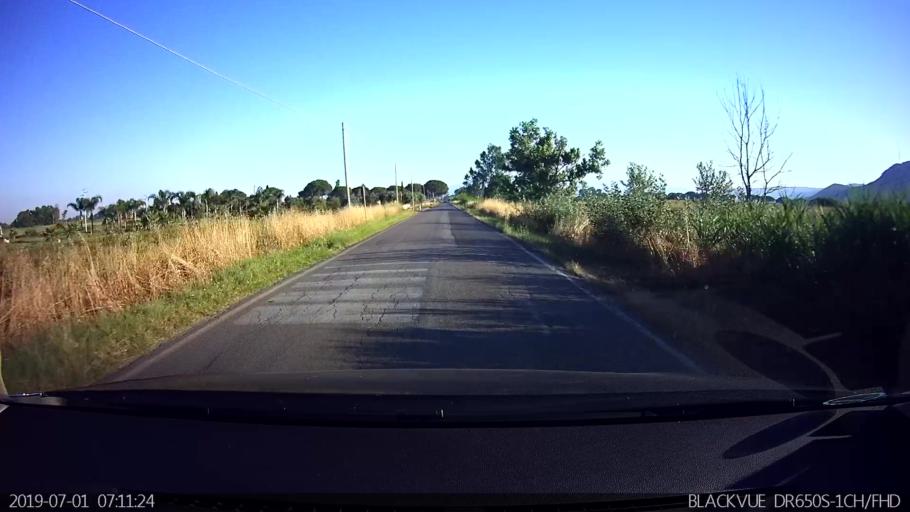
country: IT
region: Latium
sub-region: Provincia di Latina
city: Borgo Hermada
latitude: 41.3195
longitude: 13.1787
